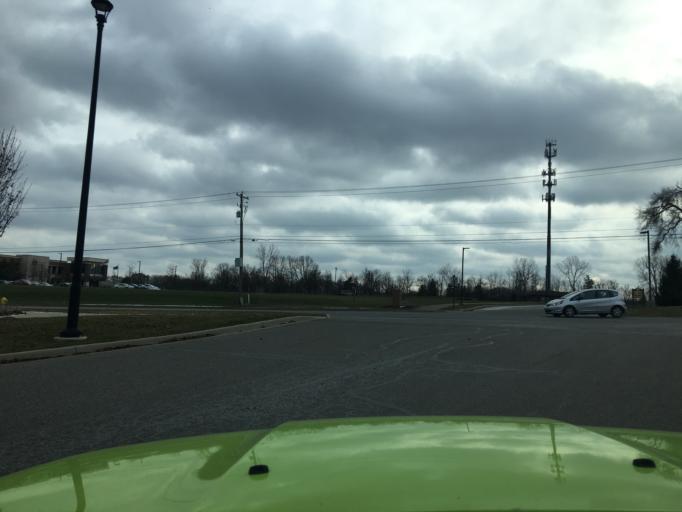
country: US
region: Michigan
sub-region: Kent County
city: Northview
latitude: 42.9991
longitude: -85.5883
